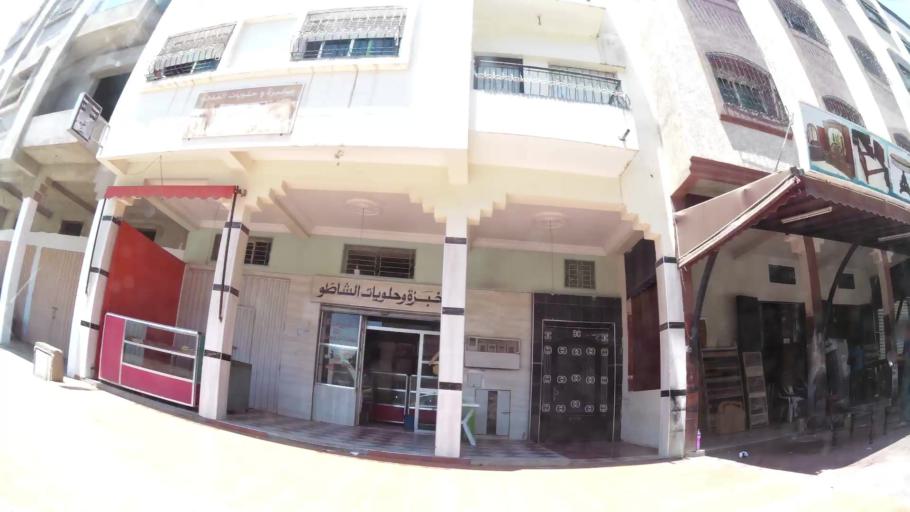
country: MA
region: Gharb-Chrarda-Beni Hssen
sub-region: Kenitra Province
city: Kenitra
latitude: 34.2514
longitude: -6.6255
